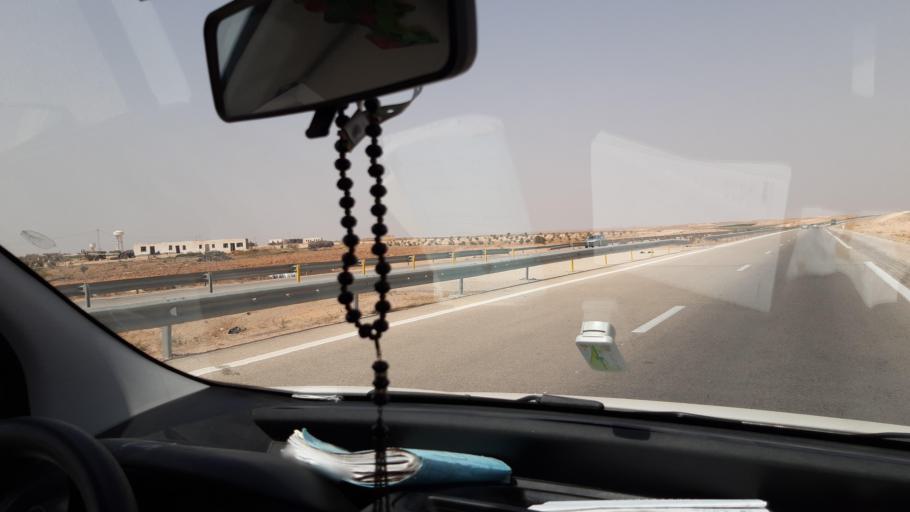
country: TN
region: Safaqis
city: Skhira
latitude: 34.2337
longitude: 9.9834
